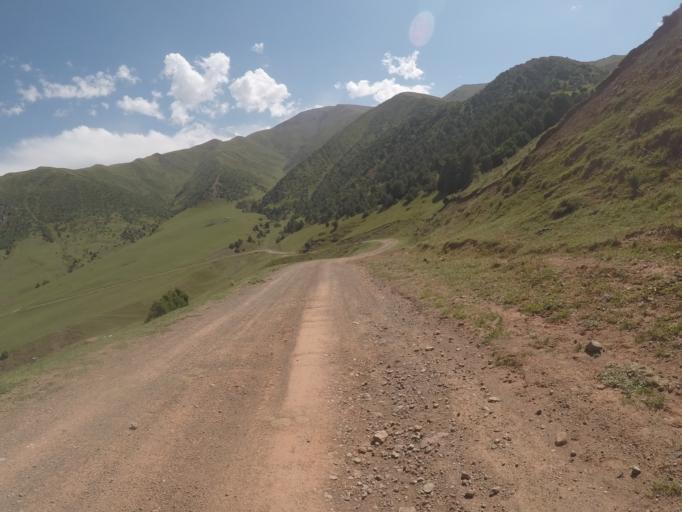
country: KG
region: Chuy
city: Bishkek
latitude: 42.6470
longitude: 74.5693
